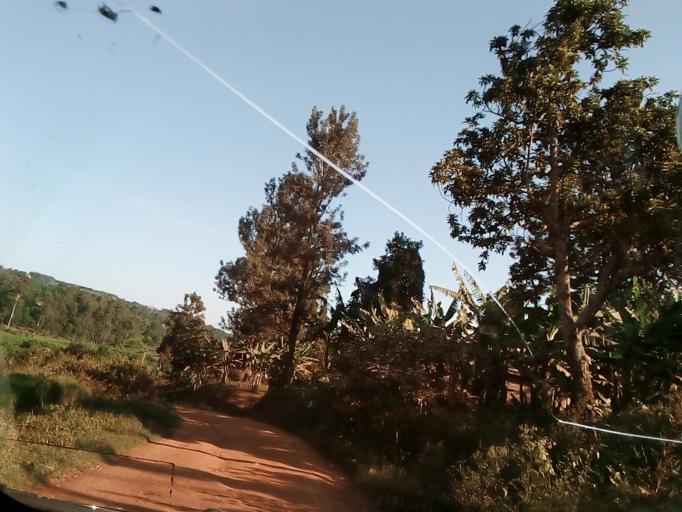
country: UG
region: Central Region
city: Masaka
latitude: -0.3288
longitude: 31.7464
